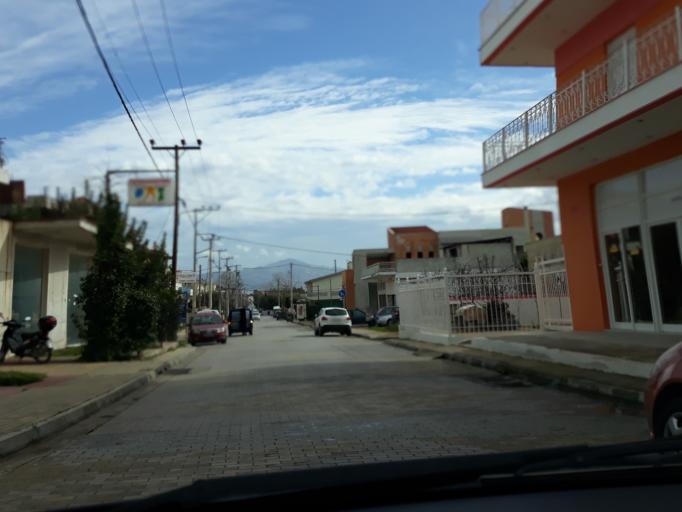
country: GR
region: Attica
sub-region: Nomarchia Dytikis Attikis
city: Ano Liosia
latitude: 38.0796
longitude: 23.7071
